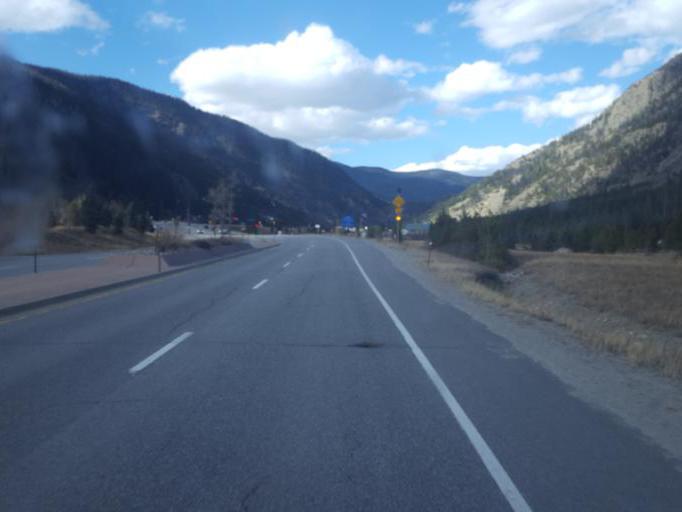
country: US
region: Colorado
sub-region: Summit County
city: Frisco
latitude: 39.5020
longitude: -106.1402
